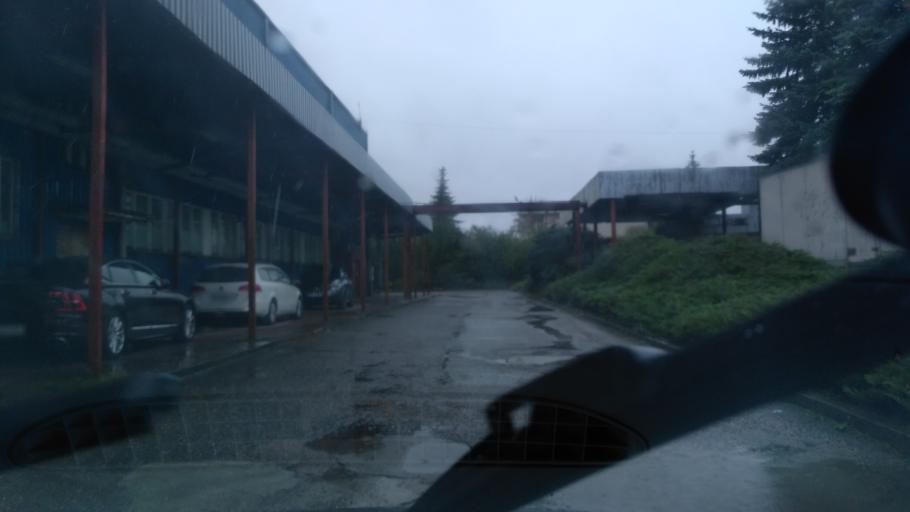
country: PL
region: Subcarpathian Voivodeship
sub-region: Powiat debicki
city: Debica
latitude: 50.0538
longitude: 21.3911
